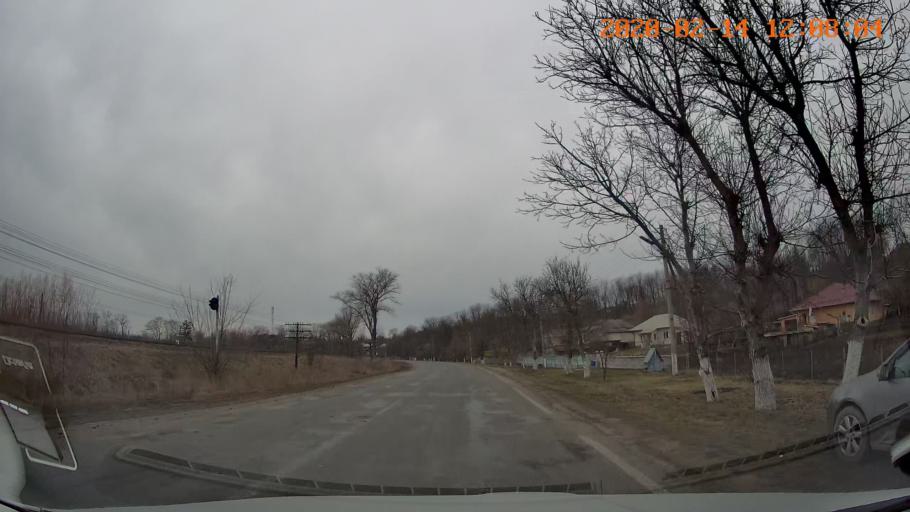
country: RO
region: Botosani
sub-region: Comuna Paltinis
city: Paltinis
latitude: 48.2697
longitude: 26.6582
